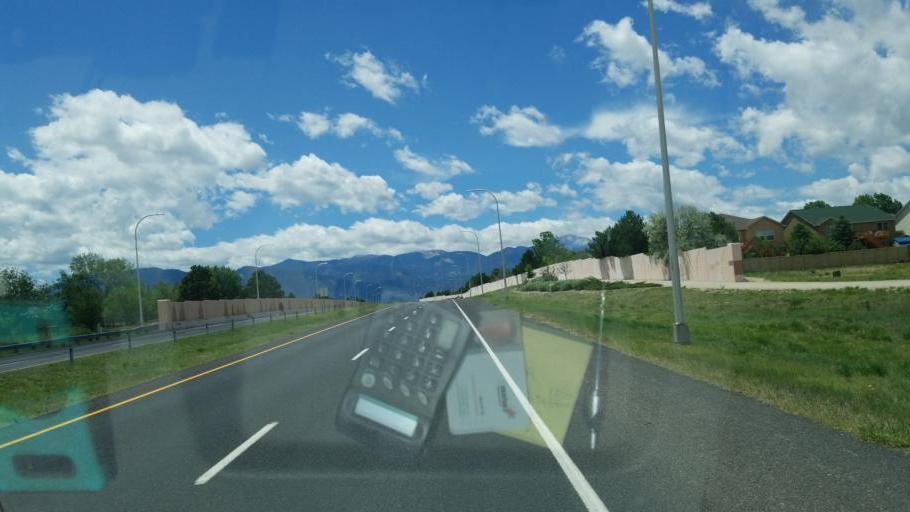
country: US
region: Colorado
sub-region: El Paso County
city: Security-Widefield
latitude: 38.7814
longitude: -104.7256
